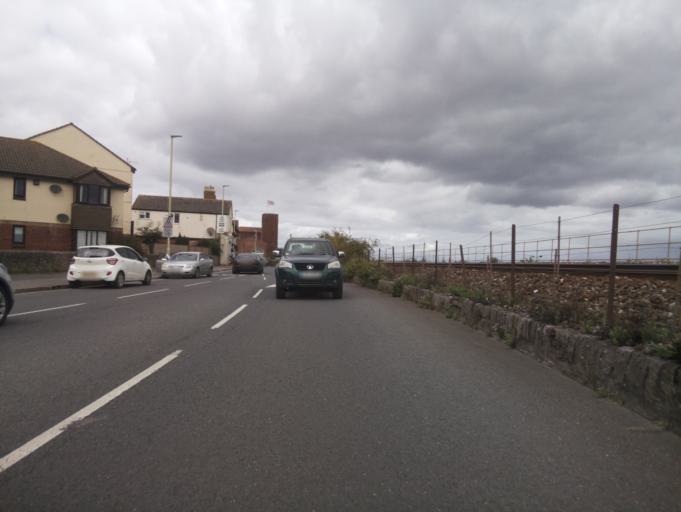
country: GB
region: England
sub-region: Devon
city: Starcross
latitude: 50.6249
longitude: -3.4464
